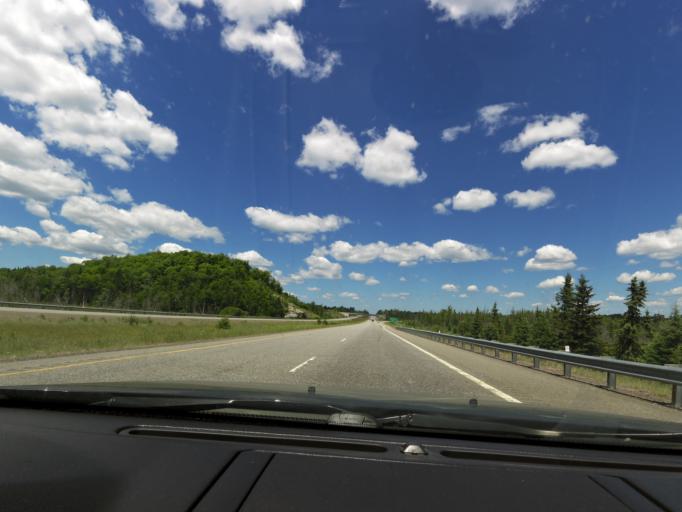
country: CA
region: Ontario
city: Huntsville
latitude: 45.5055
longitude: -79.3006
